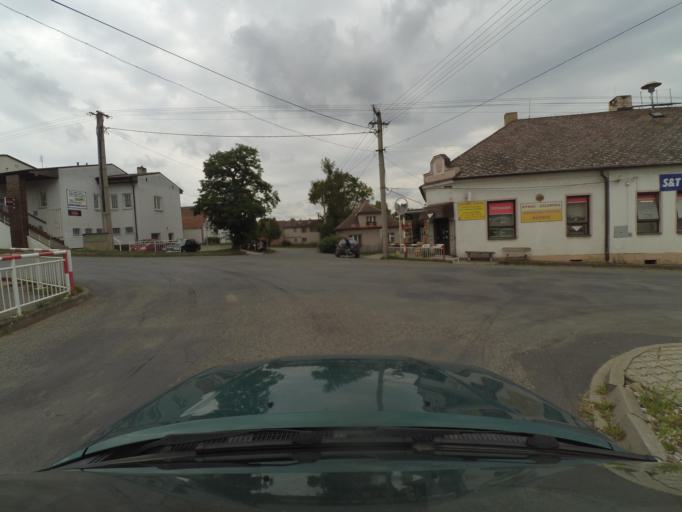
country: CZ
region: Plzensky
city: Kozlany
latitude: 49.9312
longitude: 13.5437
